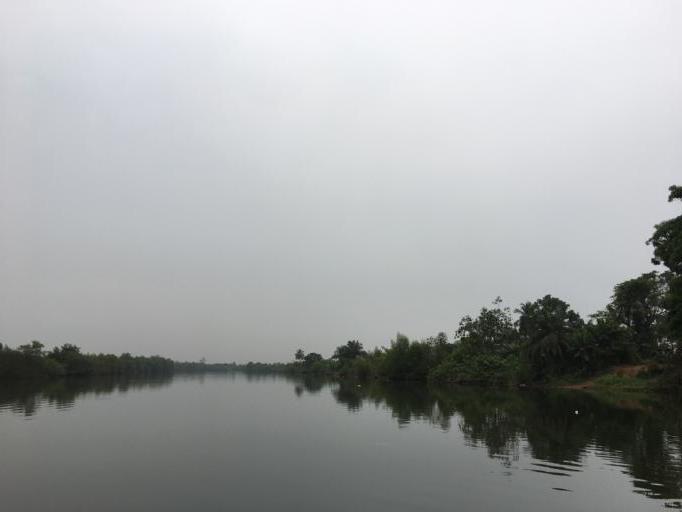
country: LR
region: Montserrado
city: Monrovia
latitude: 6.3700
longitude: -10.7777
